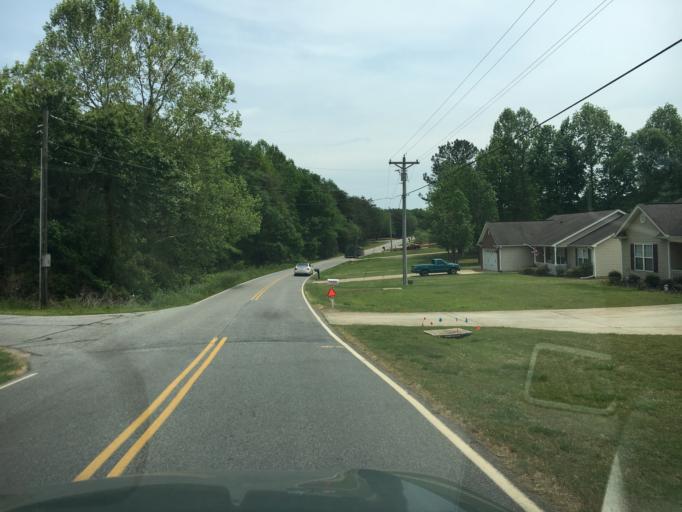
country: US
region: South Carolina
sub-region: Spartanburg County
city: Wellford
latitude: 34.9924
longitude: -82.1036
